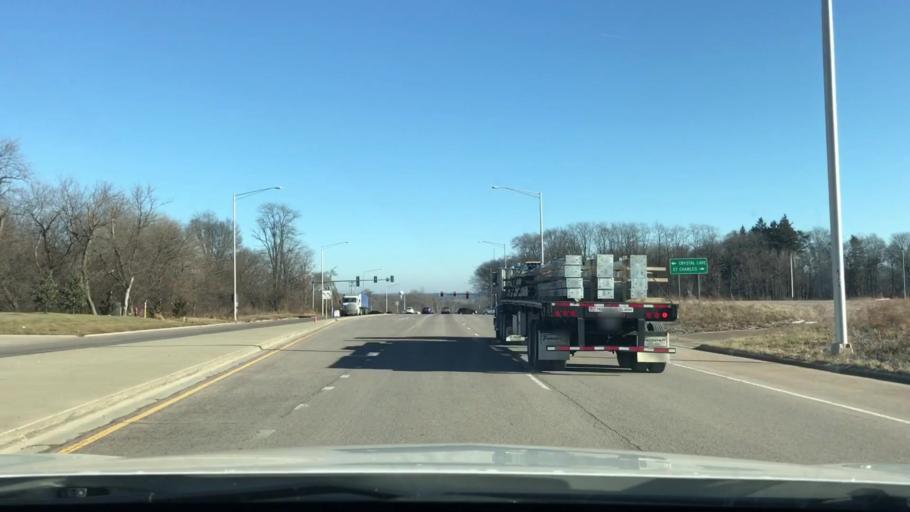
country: US
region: Illinois
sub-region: Kane County
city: Gilberts
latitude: 42.1034
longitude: -88.3376
